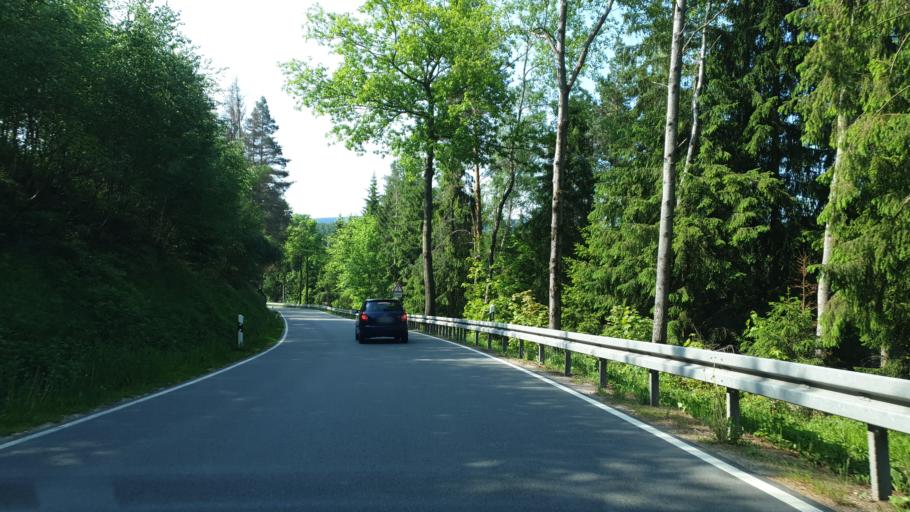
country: DE
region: Saxony
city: Eibenstock
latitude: 50.5240
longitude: 12.6118
